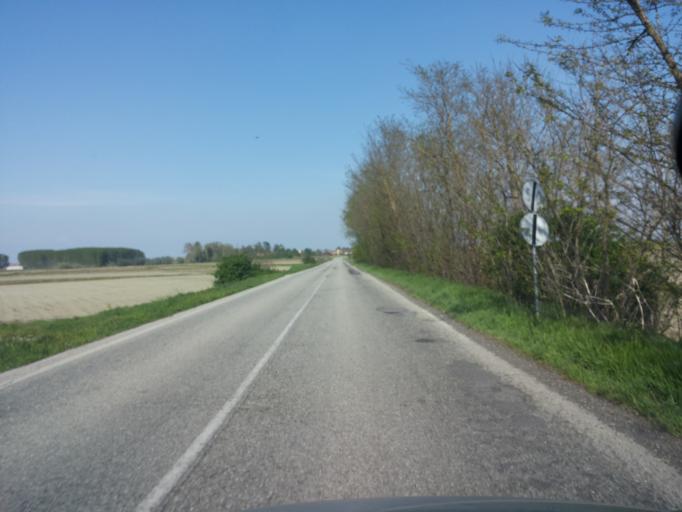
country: IT
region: Lombardy
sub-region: Provincia di Pavia
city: Langosco
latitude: 45.2087
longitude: 8.5482
